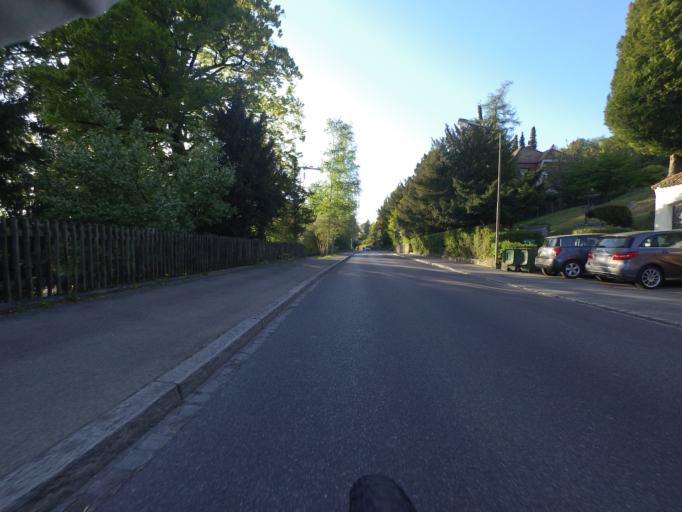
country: CH
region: Zurich
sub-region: Bezirk Winterthur
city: Stadt Winterthur (Kreis 1) / Lind
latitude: 47.5038
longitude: 8.7400
